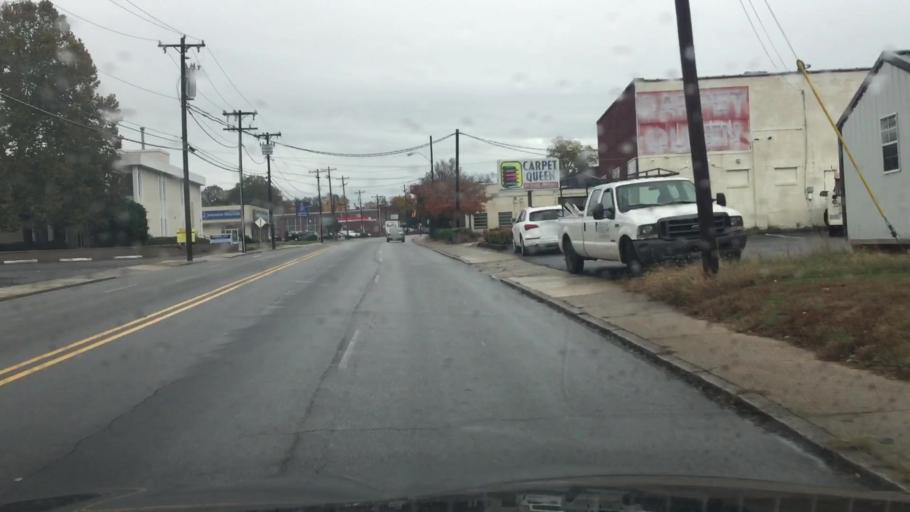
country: US
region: North Carolina
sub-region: Rowan County
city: Salisbury
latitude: 35.6742
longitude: -80.4785
